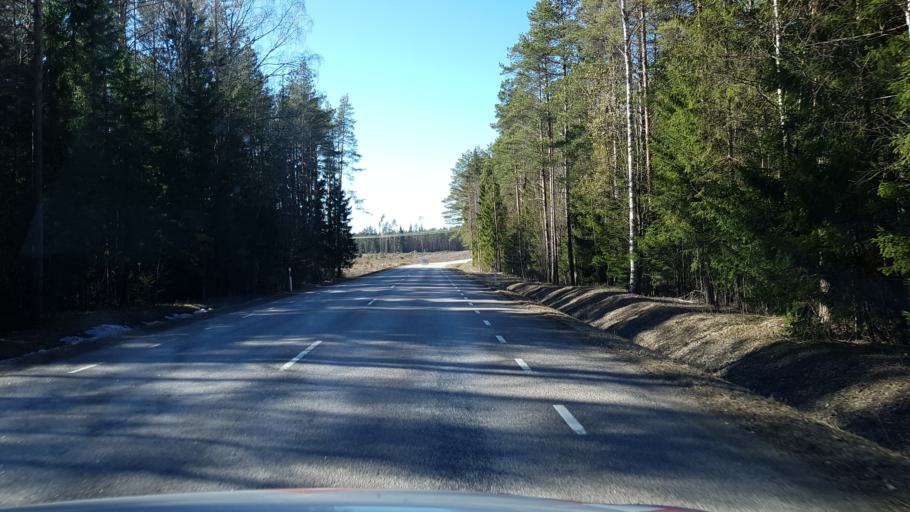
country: EE
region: Laeaene-Virumaa
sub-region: Viru-Nigula vald
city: Kunda
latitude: 59.3672
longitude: 26.6029
